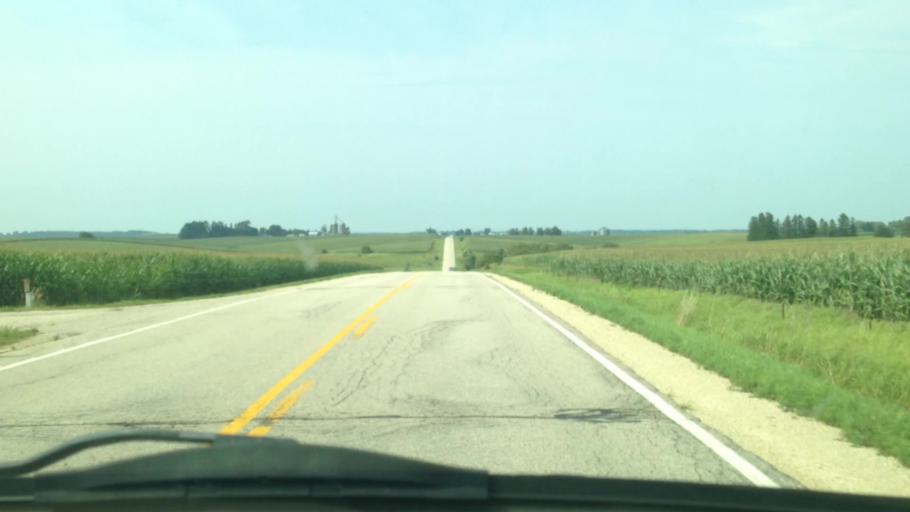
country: US
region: Minnesota
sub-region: Winona County
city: Saint Charles
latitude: 43.8698
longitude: -91.9594
